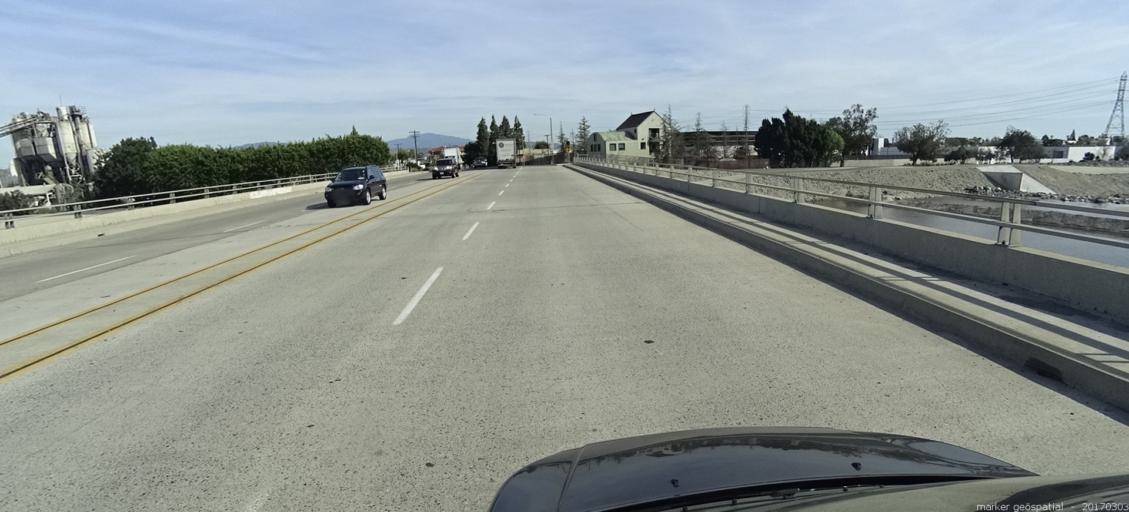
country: US
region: California
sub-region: Orange County
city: Orange
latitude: 33.8164
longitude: -117.8701
